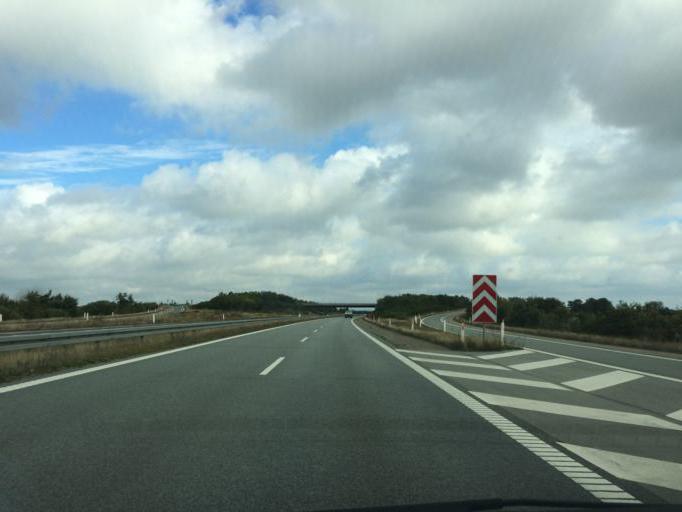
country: DK
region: North Denmark
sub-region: Alborg Kommune
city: Vodskov
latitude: 57.1336
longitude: 10.0816
